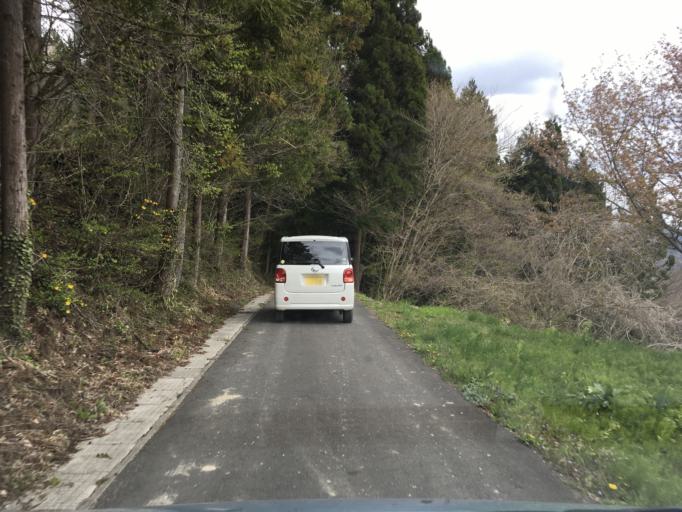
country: JP
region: Iwate
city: Ichinoseki
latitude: 38.9815
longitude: 141.1687
